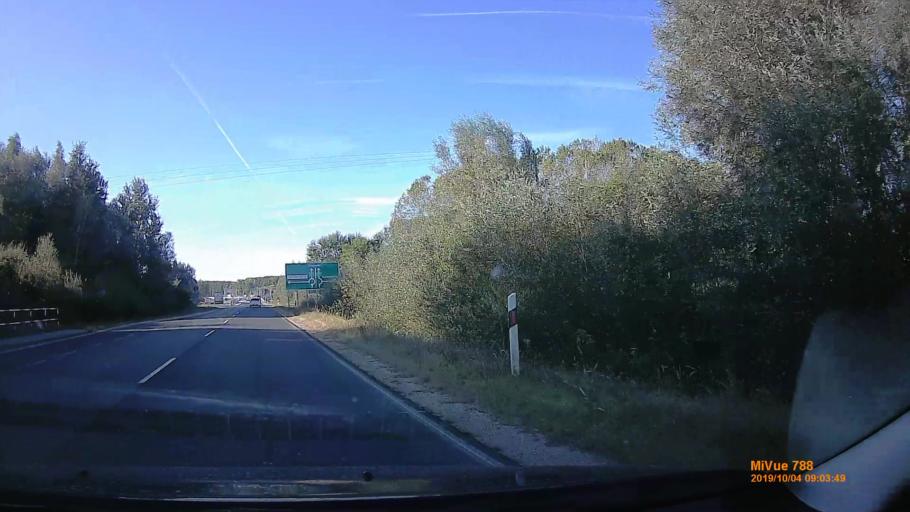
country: HU
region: Somogy
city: Karad
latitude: 46.7063
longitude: 17.7714
